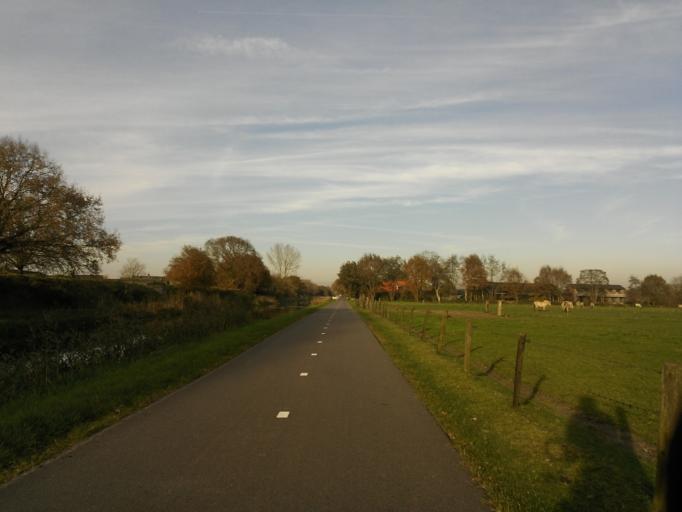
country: NL
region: Utrecht
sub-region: Gemeente Leusden
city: Leusden
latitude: 52.1110
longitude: 5.4388
